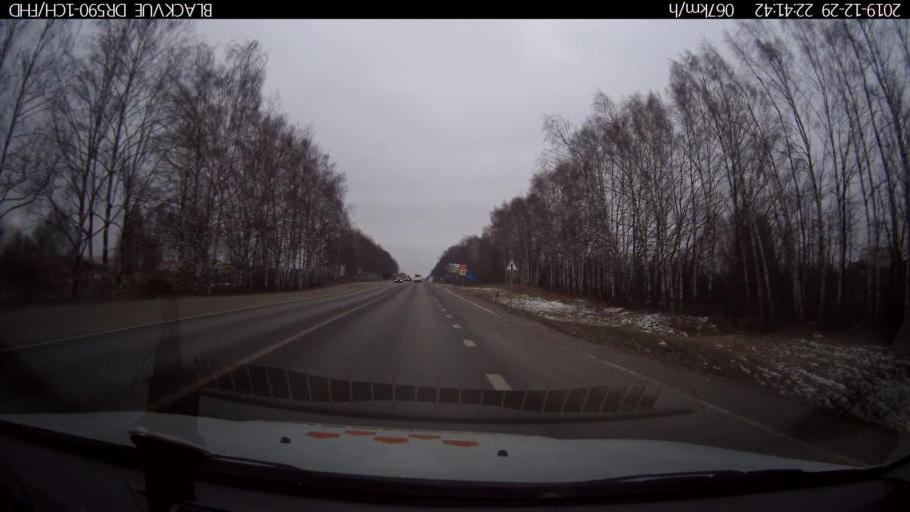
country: RU
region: Nizjnij Novgorod
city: Afonino
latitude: 56.2229
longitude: 44.0581
